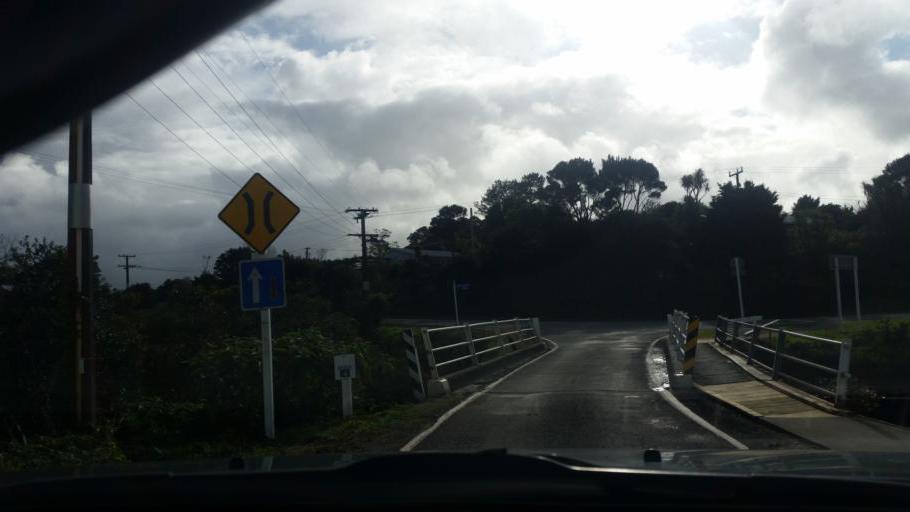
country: NZ
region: Auckland
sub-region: Auckland
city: Wellsford
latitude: -36.2487
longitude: 174.2468
